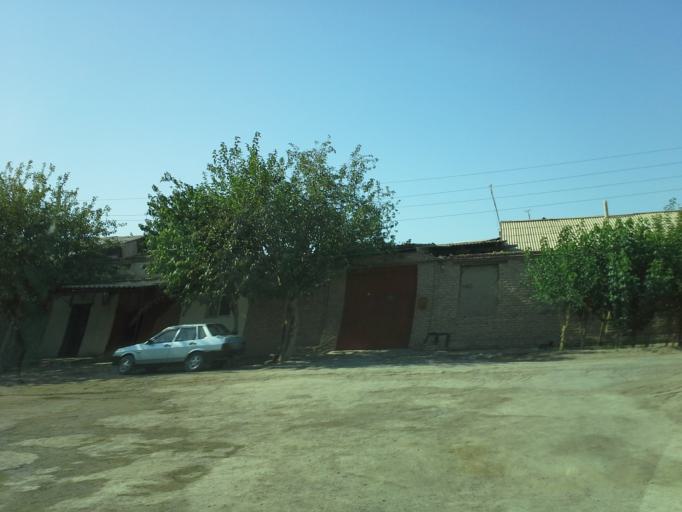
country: TM
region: Dasoguz
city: Dasoguz
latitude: 41.8248
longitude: 59.9784
